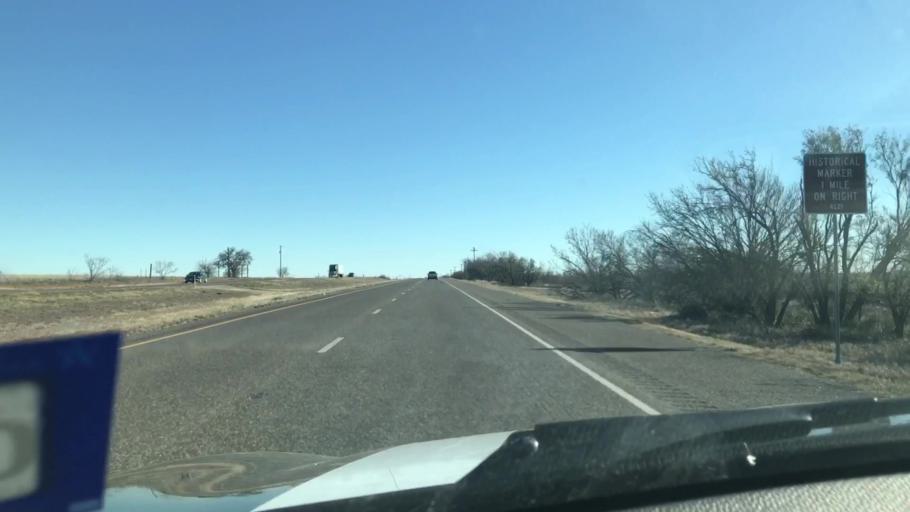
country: US
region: Texas
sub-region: Scurry County
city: Snyder
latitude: 32.8046
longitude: -100.9692
